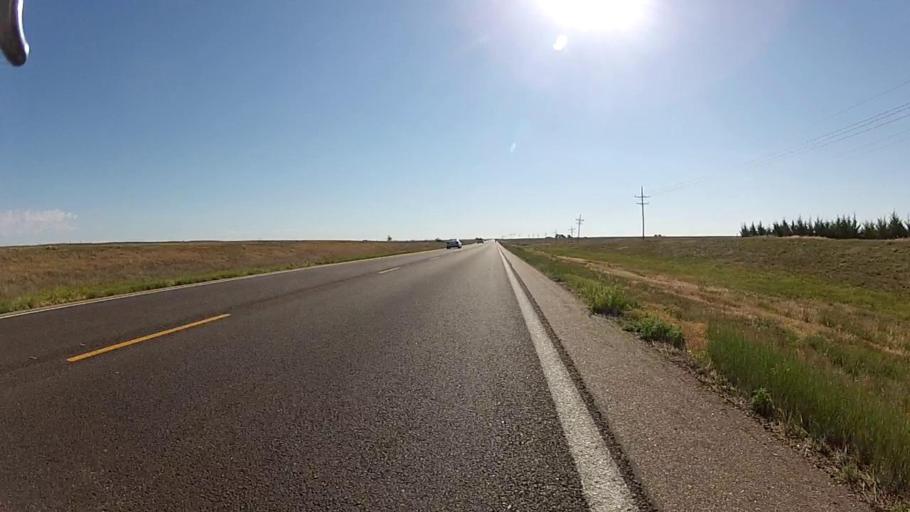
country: US
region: Kansas
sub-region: Haskell County
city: Sublette
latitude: 37.5473
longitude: -100.6134
